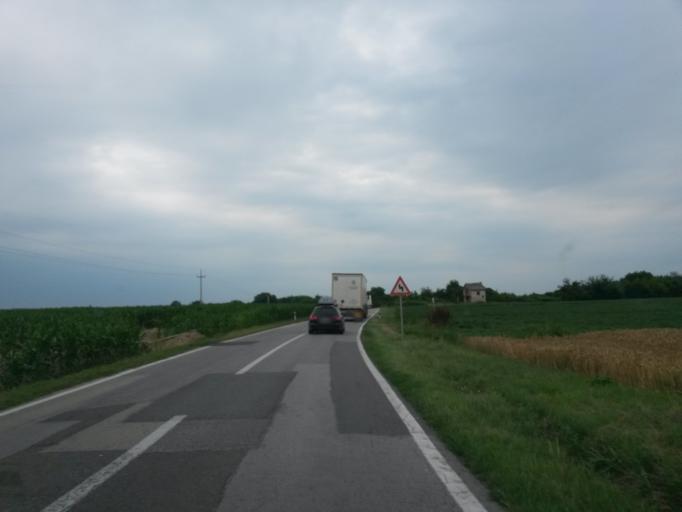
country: HR
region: Vukovarsko-Srijemska
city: Lovas
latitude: 45.2823
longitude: 19.1272
